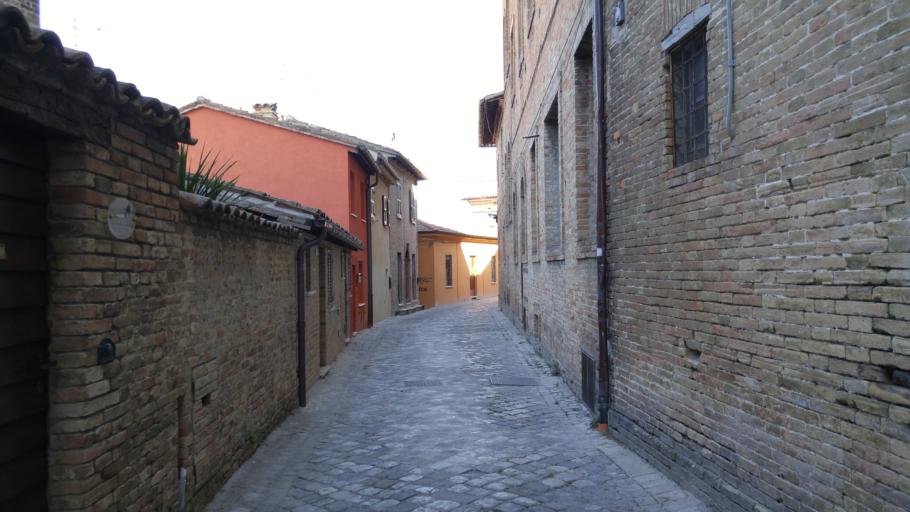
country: IT
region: The Marches
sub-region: Provincia di Pesaro e Urbino
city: Urbino
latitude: 43.7277
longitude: 12.6341
